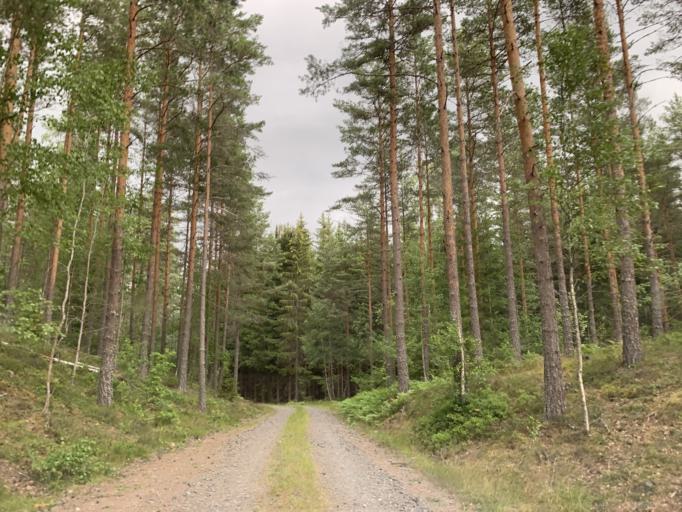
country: SE
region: Kalmar
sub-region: Vasterviks Kommun
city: Overum
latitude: 58.0246
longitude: 16.1159
